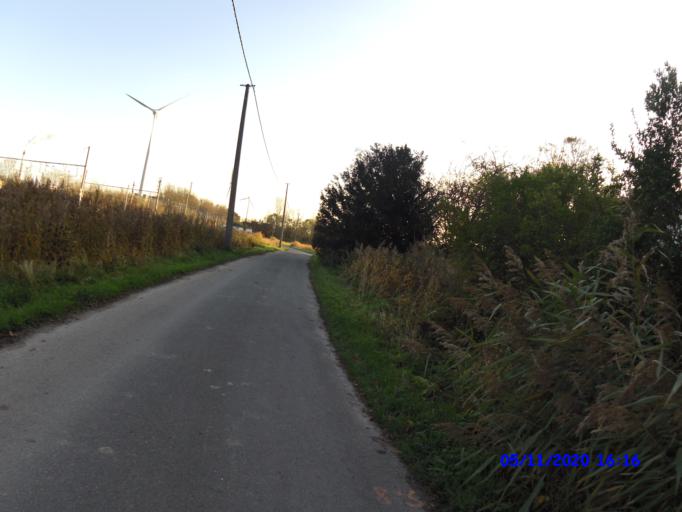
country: BE
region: Flanders
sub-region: Provincie West-Vlaanderen
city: Zuienkerke
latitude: 51.2584
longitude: 3.2031
